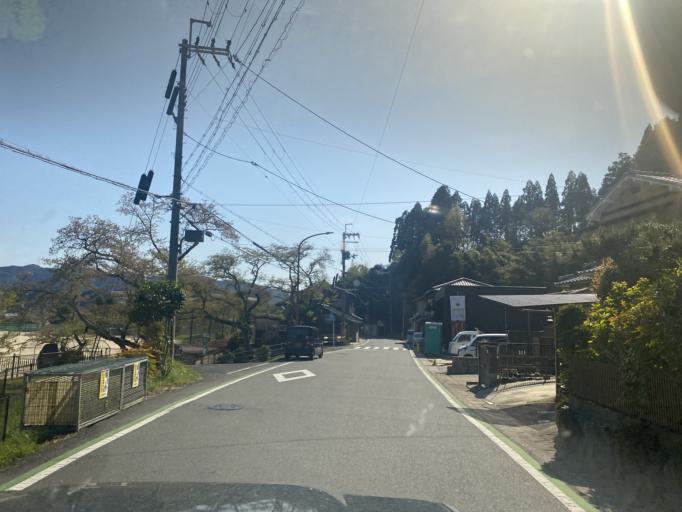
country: JP
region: Kyoto
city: Uji
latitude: 34.8577
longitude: 135.8653
